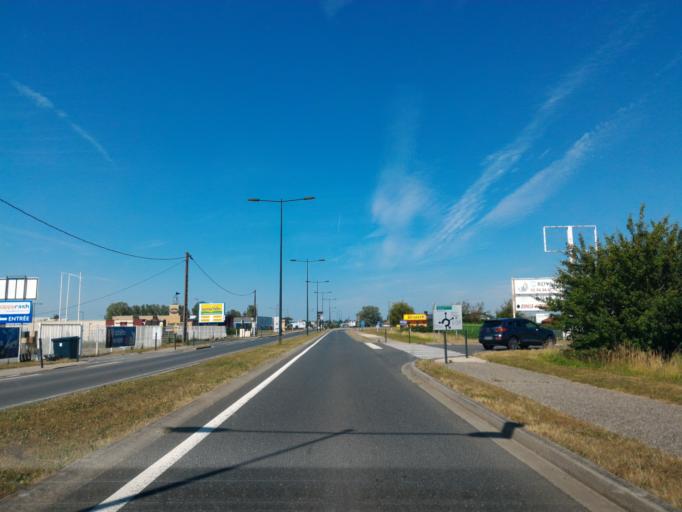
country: FR
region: Centre
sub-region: Departement de l'Indre
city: Saint-Maur
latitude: 46.7869
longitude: 1.6585
